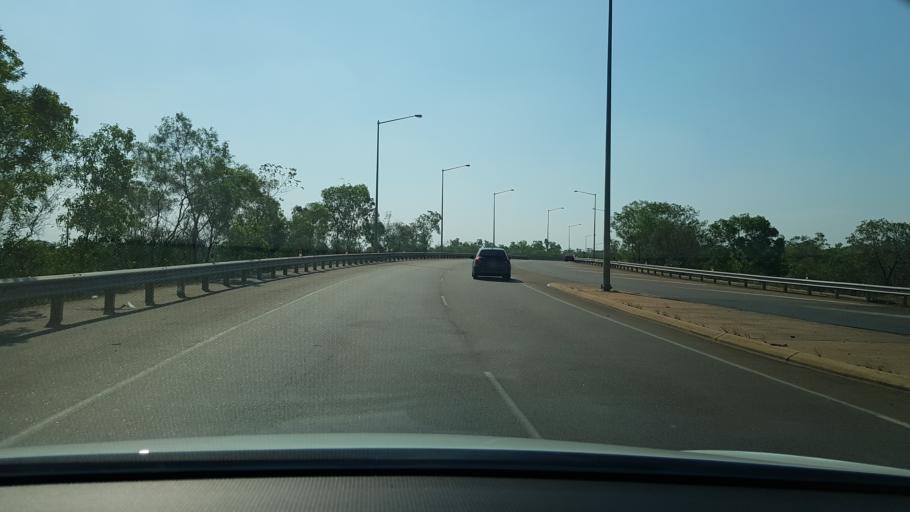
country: AU
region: Northern Territory
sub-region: Palmerston
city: Palmerston
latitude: -12.4661
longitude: 130.9755
